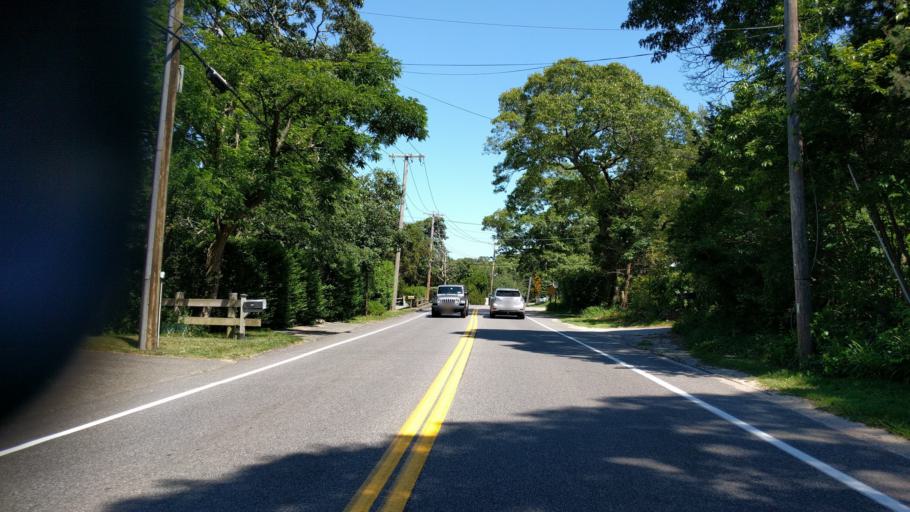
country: US
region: New York
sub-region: Suffolk County
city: Noyack
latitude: 40.9949
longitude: -72.3342
